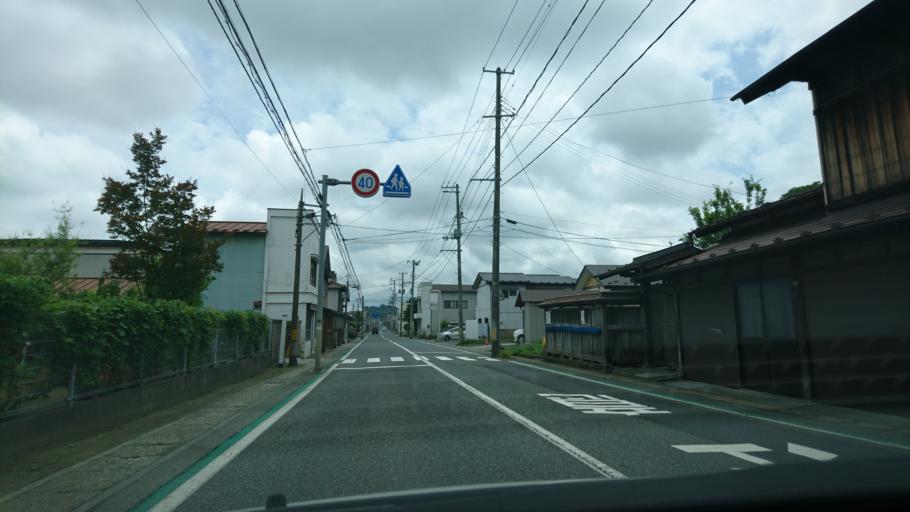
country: JP
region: Iwate
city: Ichinoseki
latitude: 38.9478
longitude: 141.1300
